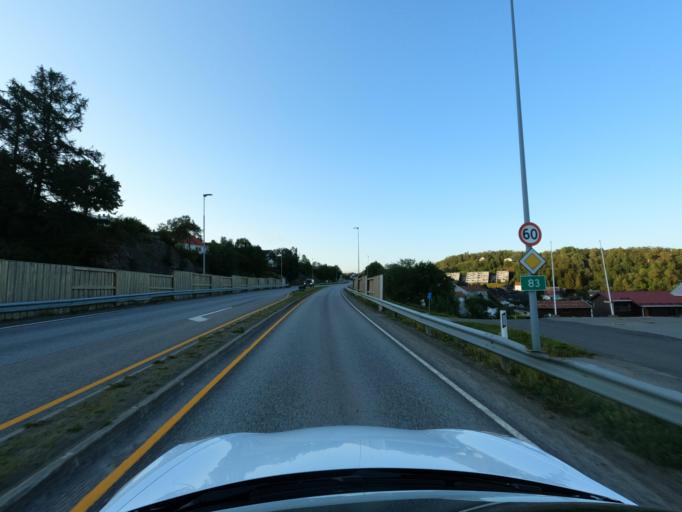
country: NO
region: Troms
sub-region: Harstad
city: Harstad
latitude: 68.7736
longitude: 16.5599
